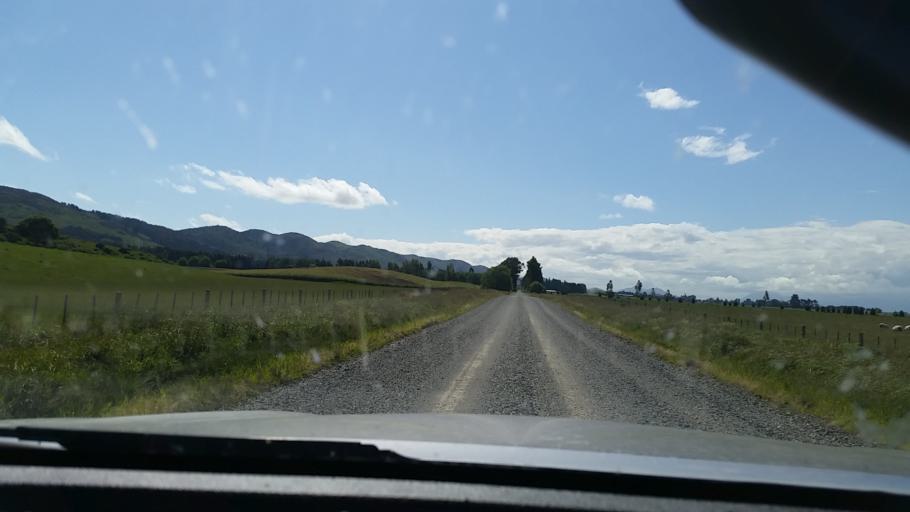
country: NZ
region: Southland
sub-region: Southland District
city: Winton
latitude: -45.8932
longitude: 168.5355
